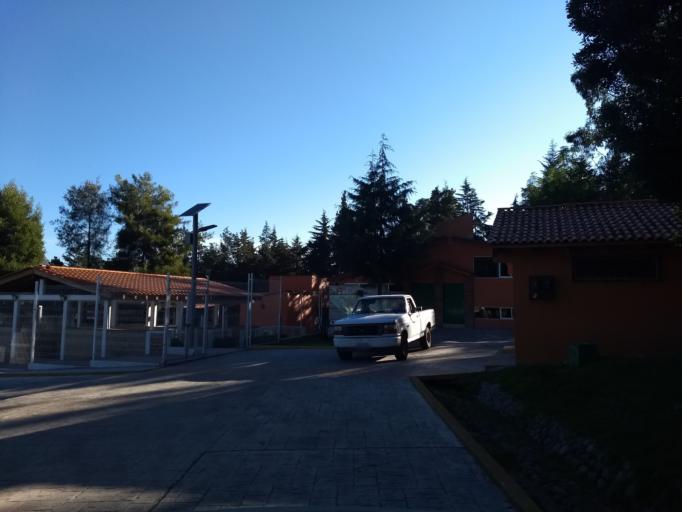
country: MX
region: Mexico
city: San Marcos Yachihuacaltepec
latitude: 19.3115
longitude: -99.6858
